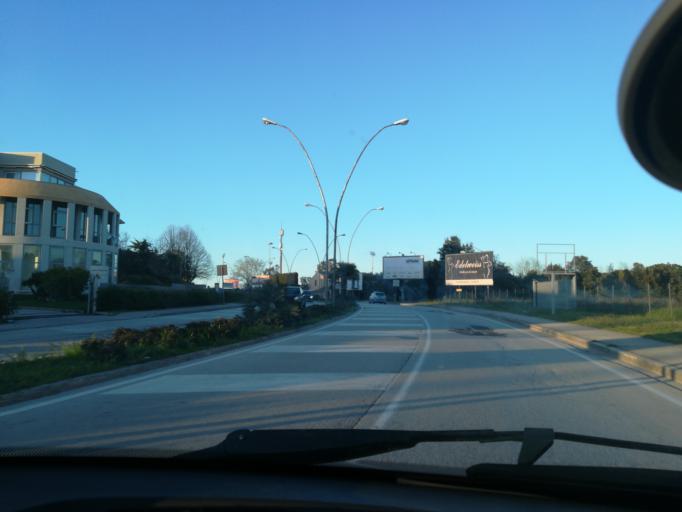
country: IT
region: The Marches
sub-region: Provincia di Macerata
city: Portocivitanova
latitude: 43.2945
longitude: 13.7357
